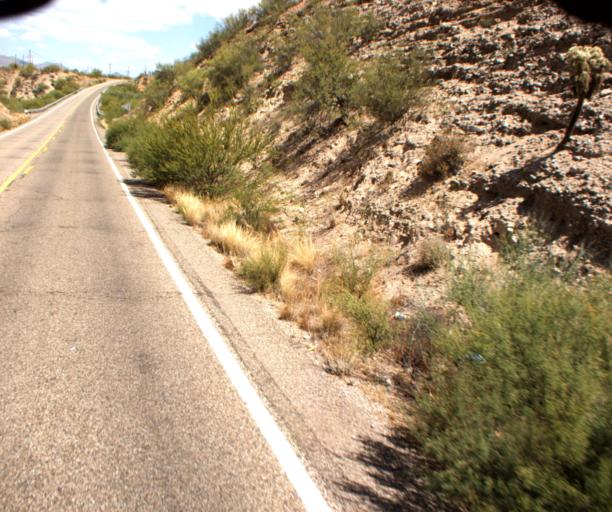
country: US
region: Arizona
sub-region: Pinal County
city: Kearny
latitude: 33.0735
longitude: -110.9198
